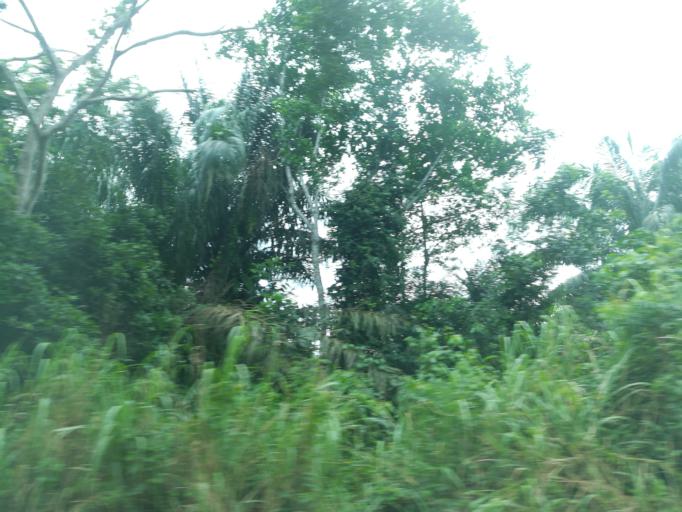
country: NG
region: Lagos
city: Ejirin
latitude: 6.6559
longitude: 3.8018
